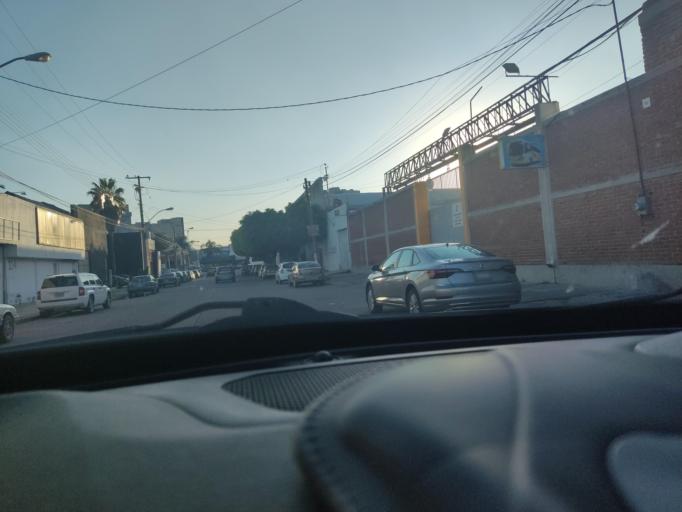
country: MX
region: Guanajuato
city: Leon
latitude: 21.1034
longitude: -101.6353
